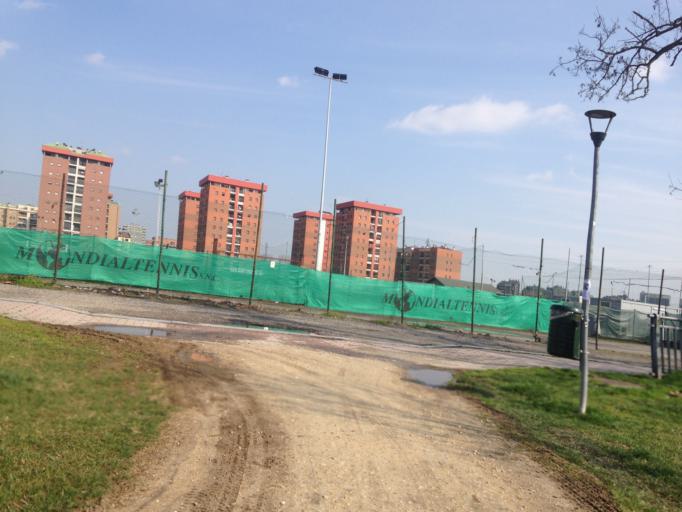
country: IT
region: Lombardy
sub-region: Citta metropolitana di Milano
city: Rozzano
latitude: 45.4238
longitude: 9.1706
